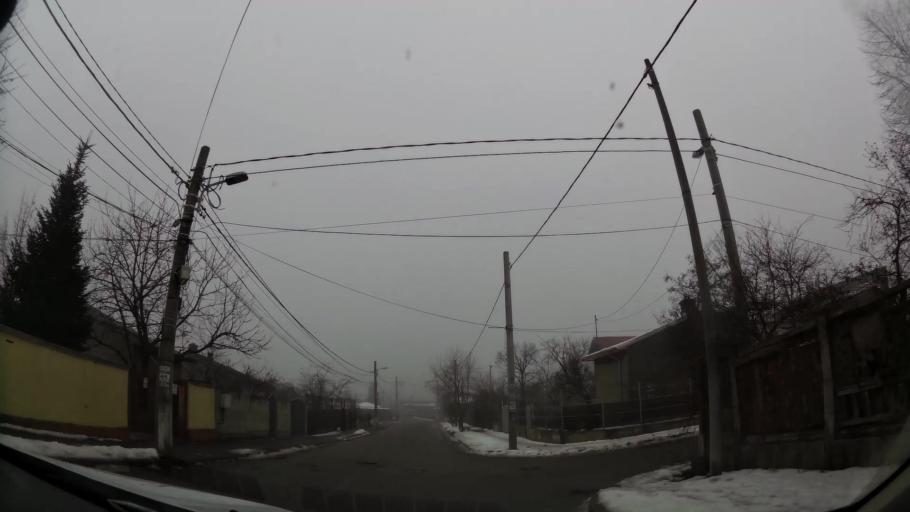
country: RO
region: Ilfov
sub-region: Comuna Chiajna
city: Rosu
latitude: 44.4748
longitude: 26.0053
